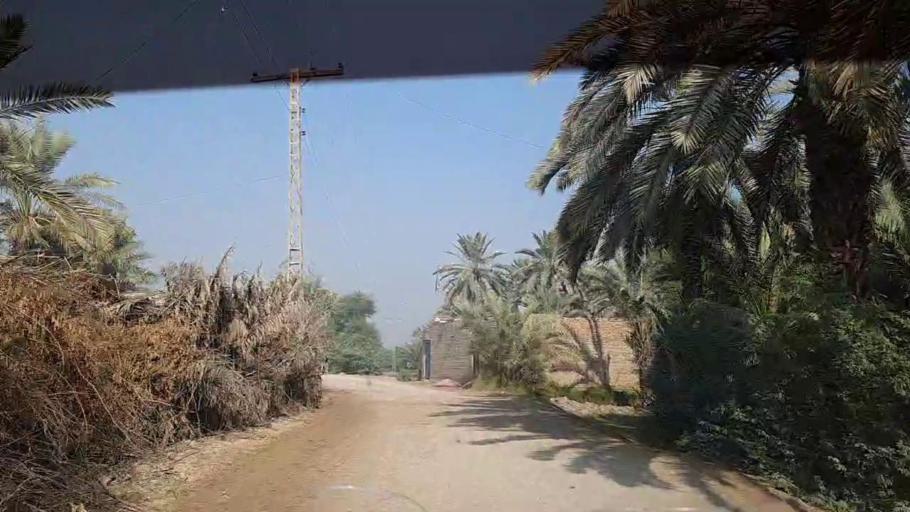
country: PK
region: Sindh
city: Khairpur
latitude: 27.4986
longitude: 68.7370
